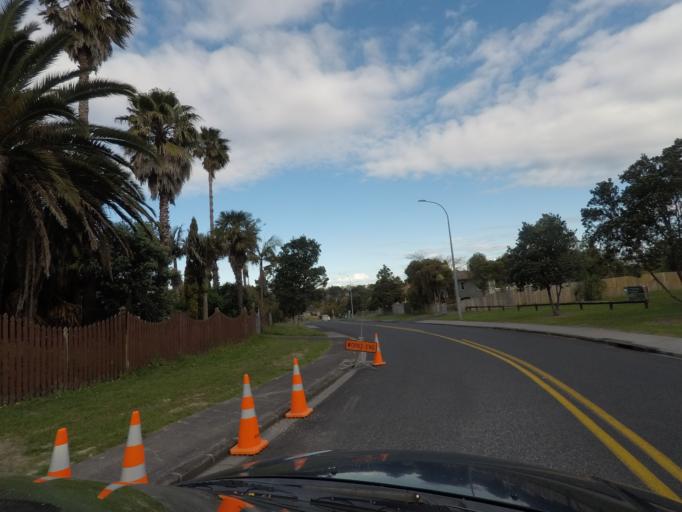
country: NZ
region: Auckland
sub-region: Auckland
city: Rosebank
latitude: -36.8858
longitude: 174.6488
